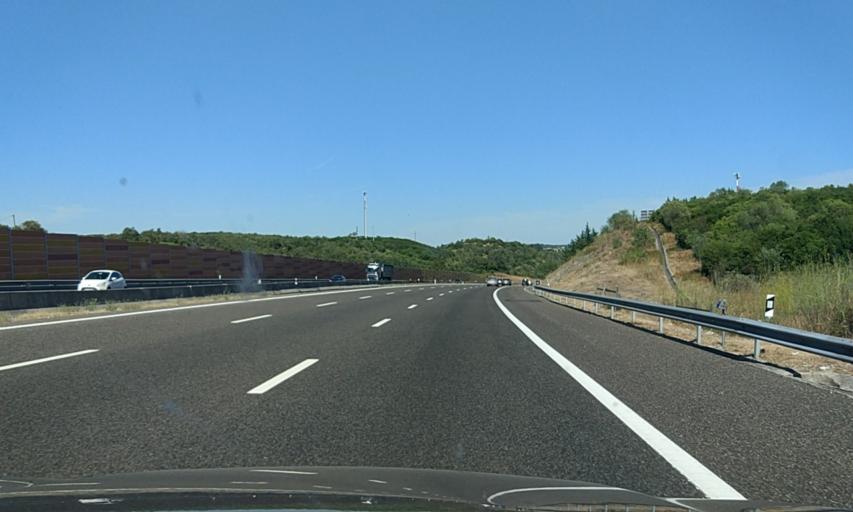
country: PT
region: Santarem
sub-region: Santarem
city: Santarem
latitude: 39.2341
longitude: -8.7590
